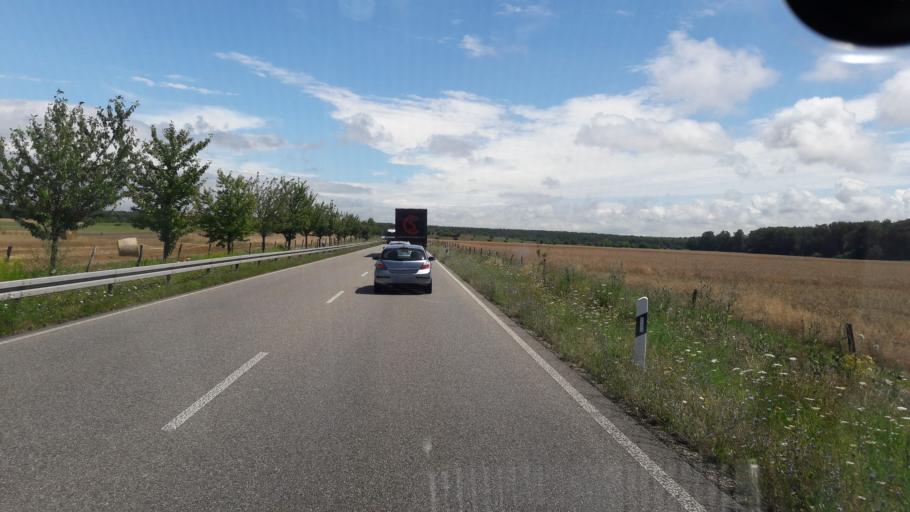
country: DE
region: Baden-Wuerttemberg
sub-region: Karlsruhe Region
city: Graben-Neudorf
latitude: 49.1419
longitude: 8.4643
